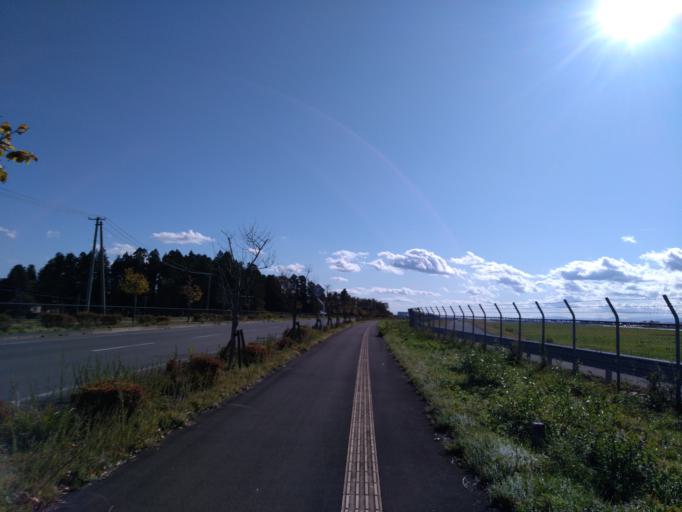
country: JP
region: Iwate
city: Hanamaki
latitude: 39.4380
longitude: 141.1405
